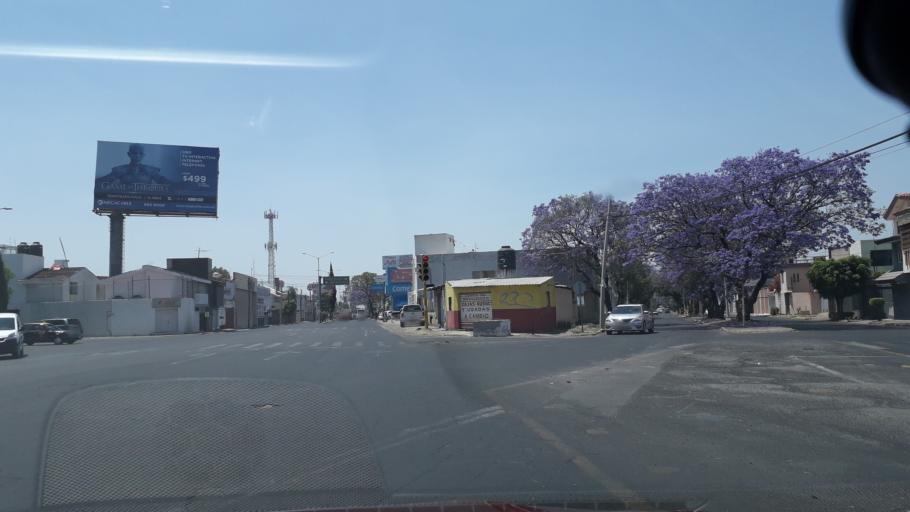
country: MX
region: Puebla
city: Puebla
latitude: 19.0236
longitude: -98.1918
